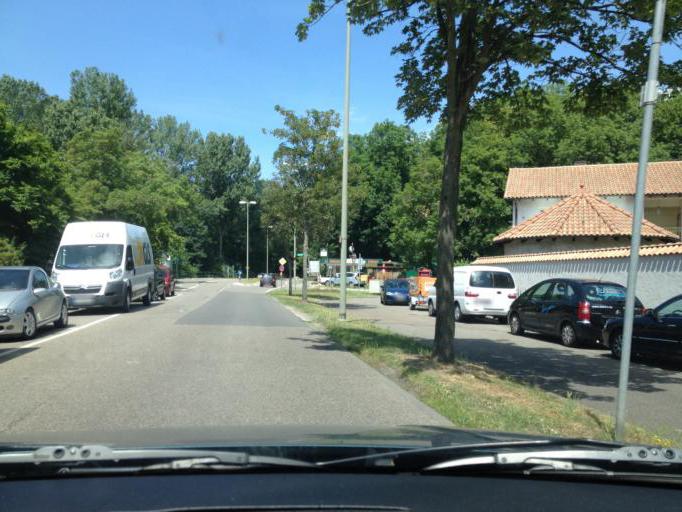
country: DE
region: Rheinland-Pfalz
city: Neuhofen
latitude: 49.4305
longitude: 8.4211
